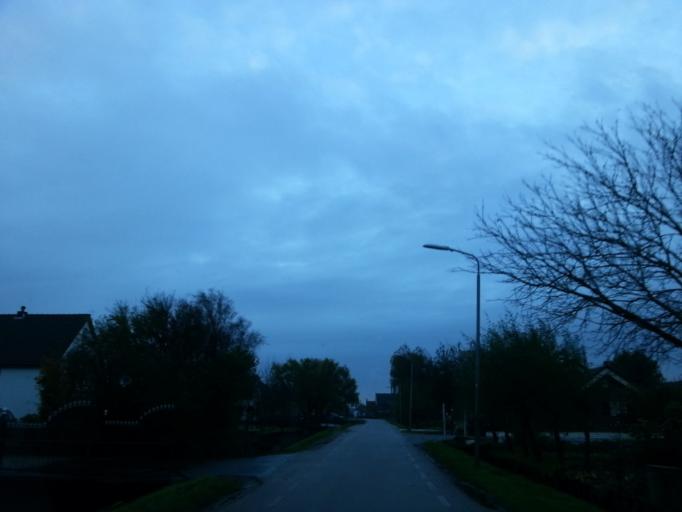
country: NL
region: South Holland
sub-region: Gemeente Pijnacker-Nootdorp
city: Pijnacker
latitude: 52.0095
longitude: 4.4261
